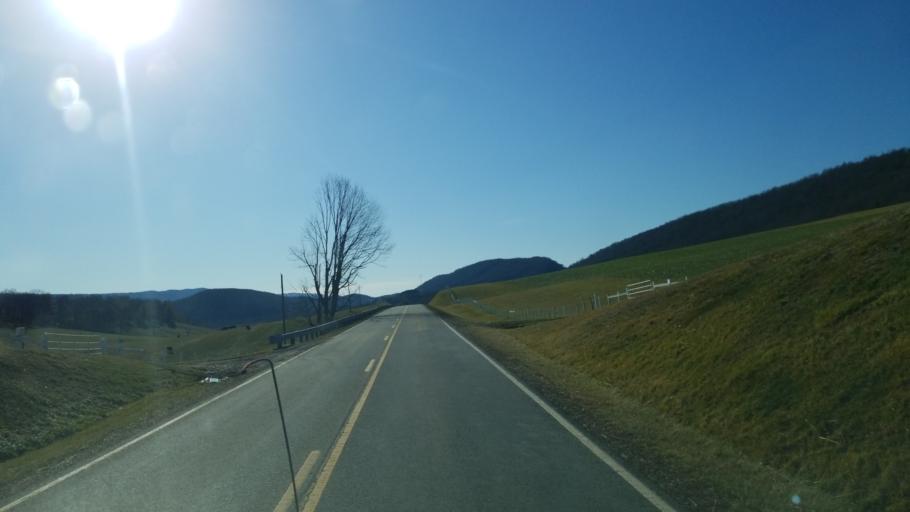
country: US
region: Virginia
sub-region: Pulaski County
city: Pulaski
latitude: 37.1781
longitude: -80.8739
